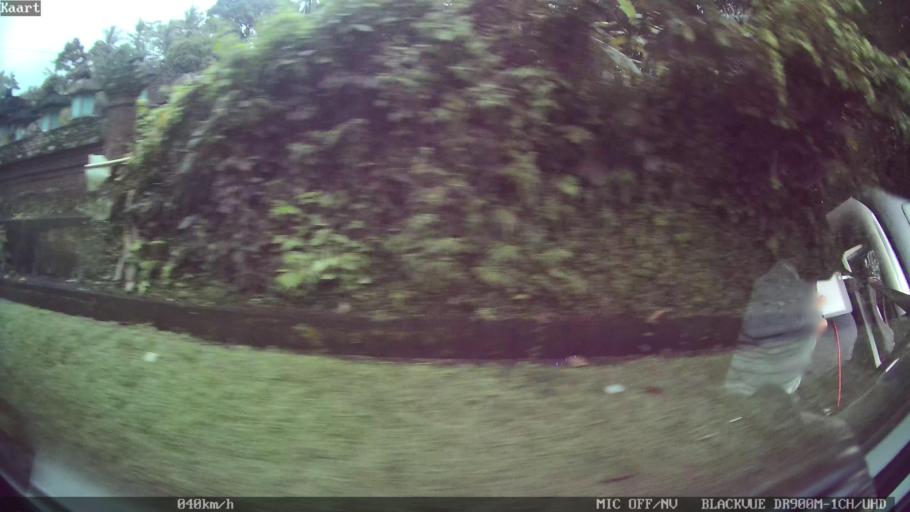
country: ID
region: Bali
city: Pegongan
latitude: -8.4816
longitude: 115.2278
